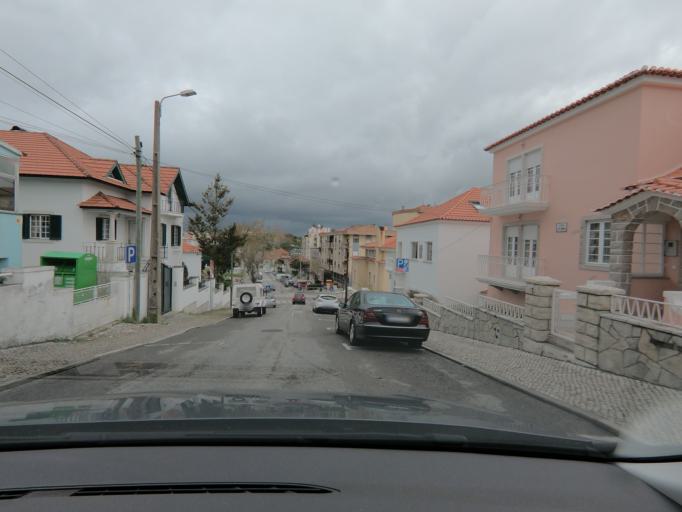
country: PT
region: Lisbon
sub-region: Sintra
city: Sintra
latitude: 38.7998
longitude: -9.3801
